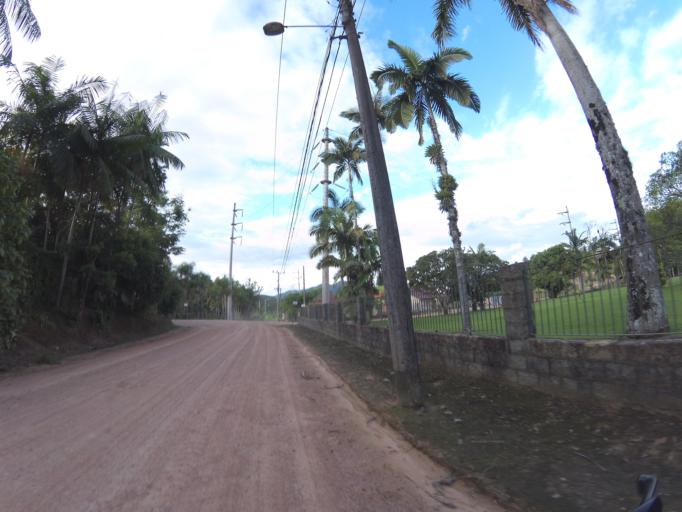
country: BR
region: Santa Catarina
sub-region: Pomerode
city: Pomerode
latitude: -26.7996
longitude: -49.1586
